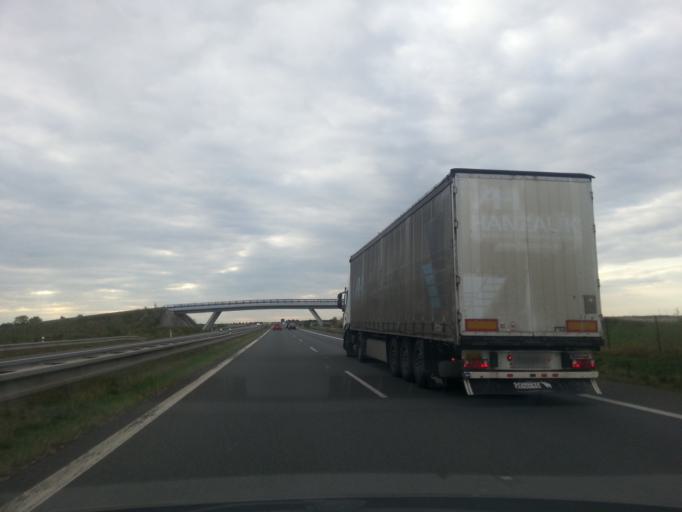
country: CZ
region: Central Bohemia
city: Jenec
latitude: 50.0950
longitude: 14.2374
